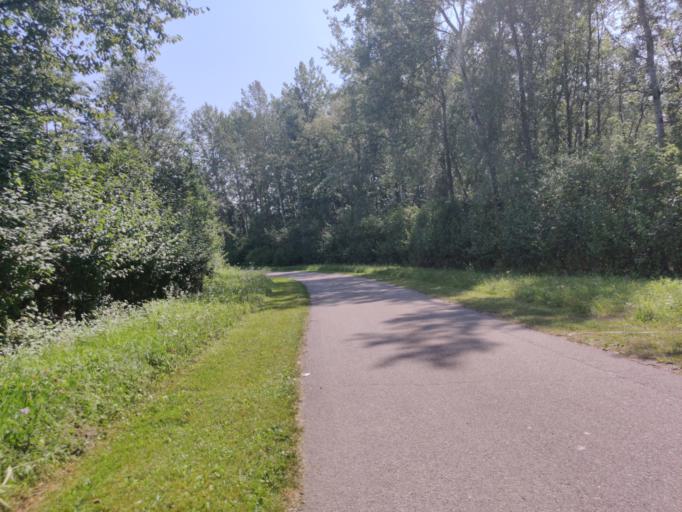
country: AT
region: Upper Austria
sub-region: Politischer Bezirk Urfahr-Umgebung
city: Ottensheim
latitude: 48.3147
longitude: 14.1497
